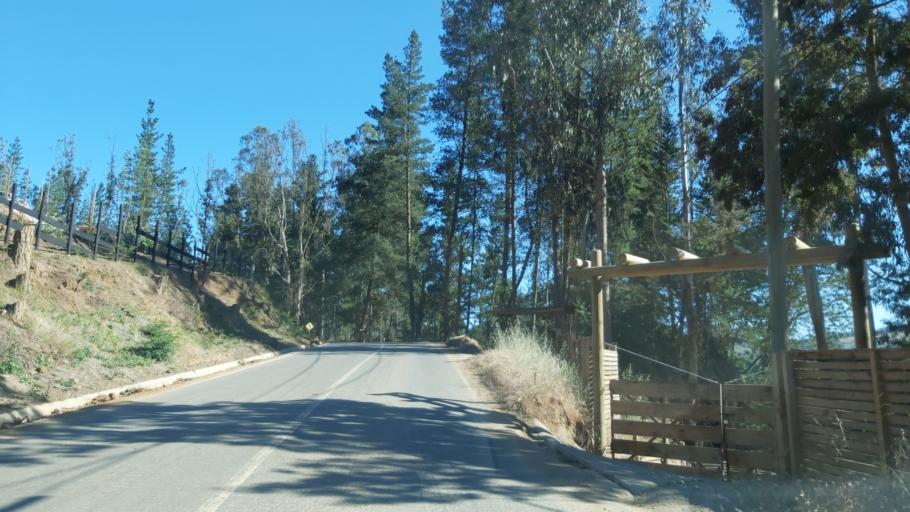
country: CL
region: Maule
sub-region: Provincia de Talca
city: Constitucion
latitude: -34.8472
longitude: -72.0470
